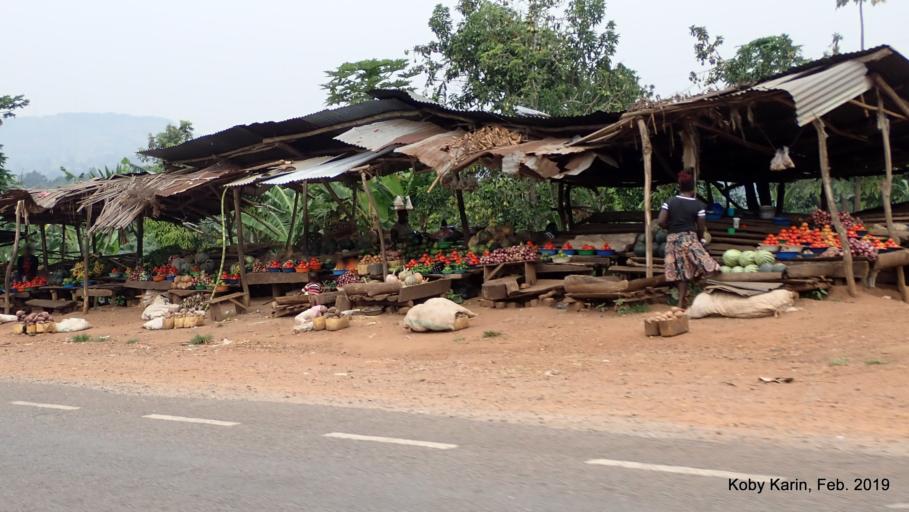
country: UG
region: Central Region
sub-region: Mityana District
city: Mityana
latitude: 0.3806
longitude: 32.1763
